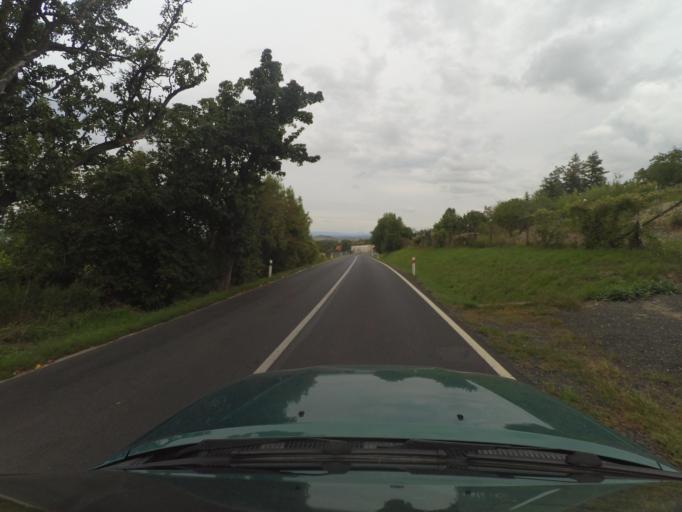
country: CZ
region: Ustecky
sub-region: Okres Louny
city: Louny
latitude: 50.3088
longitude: 13.7928
